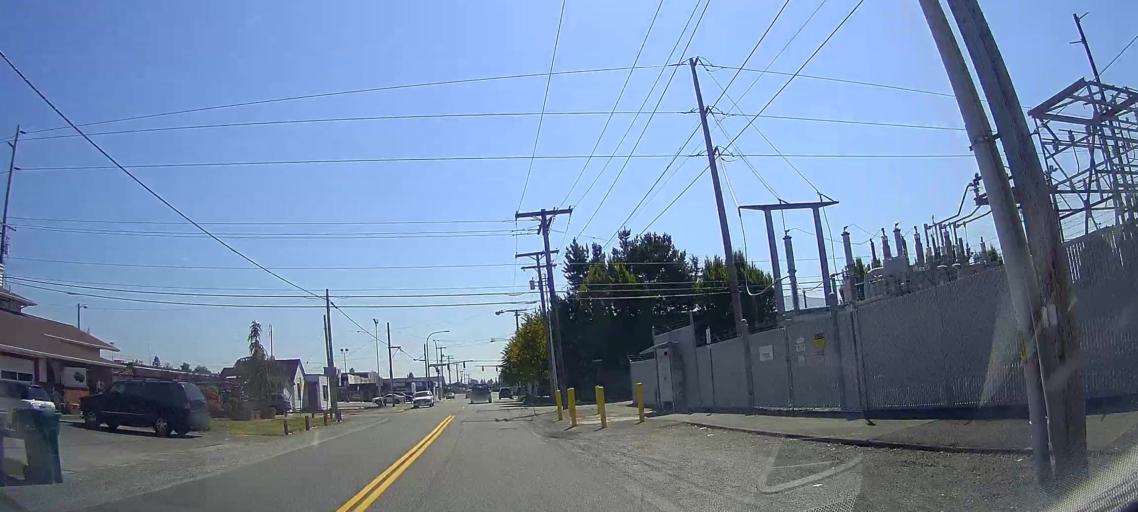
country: US
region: Washington
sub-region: Skagit County
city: Burlington
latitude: 48.4767
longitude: -122.3308
